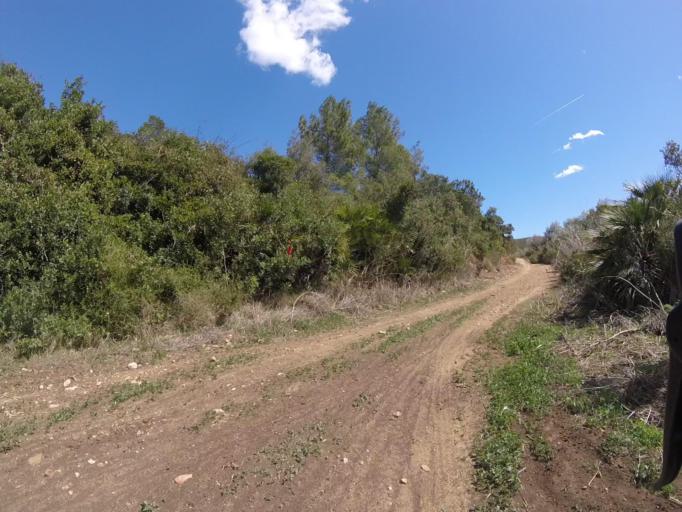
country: ES
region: Valencia
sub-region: Provincia de Castello
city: Cabanes
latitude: 40.1616
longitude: 0.1070
